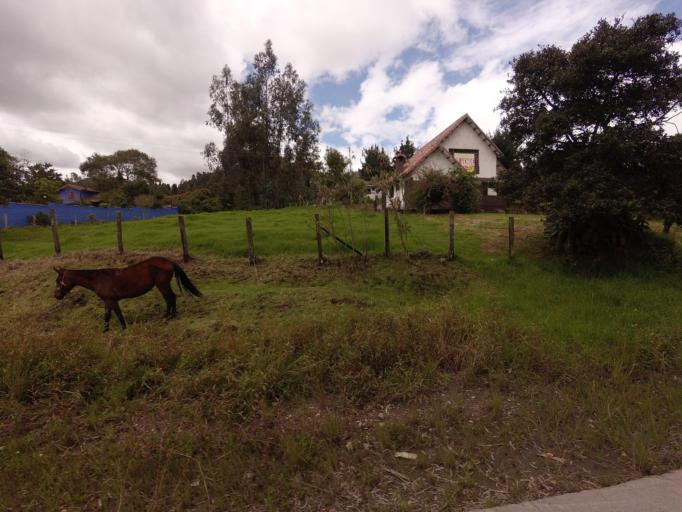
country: CO
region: Cundinamarca
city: Tabio
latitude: 4.9473
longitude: -74.0708
